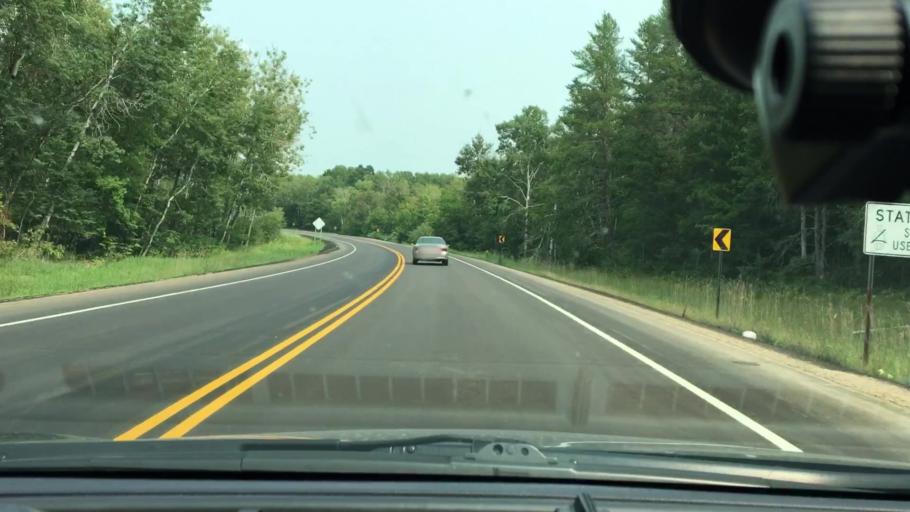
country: US
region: Minnesota
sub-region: Crow Wing County
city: Nisswa
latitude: 46.5218
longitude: -94.2760
